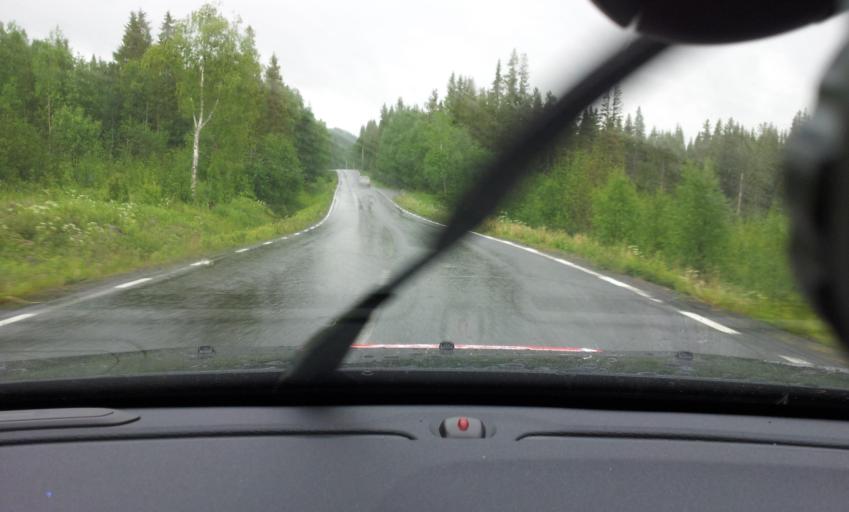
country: SE
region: Jaemtland
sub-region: Are Kommun
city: Are
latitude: 63.3142
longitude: 13.1516
